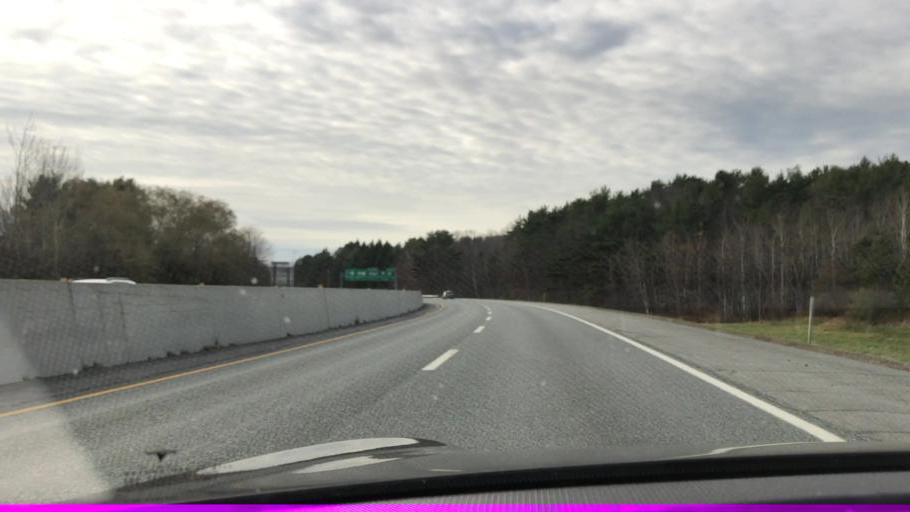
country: US
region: Maine
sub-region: Penobscot County
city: Bangor
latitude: 44.8041
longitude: -68.7990
